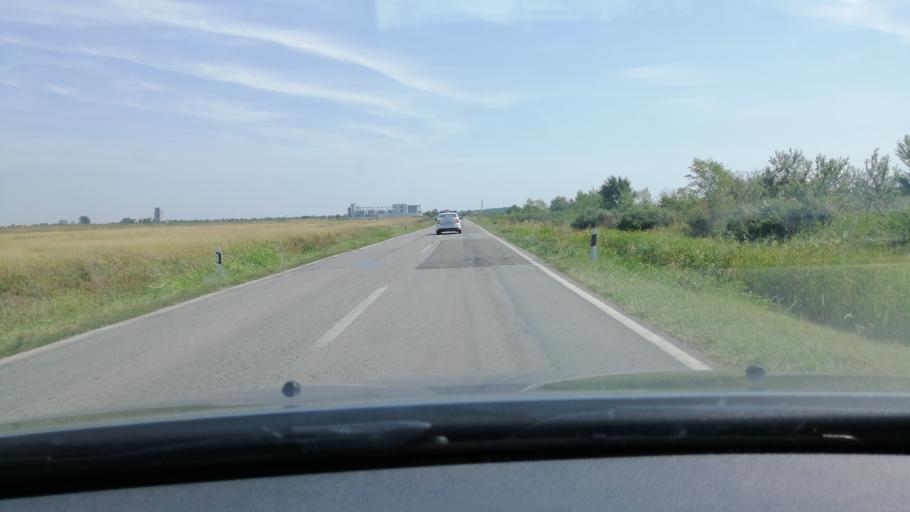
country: RS
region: Autonomna Pokrajina Vojvodina
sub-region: Srednjebanatski Okrug
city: Secanj
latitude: 45.3736
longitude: 20.7436
